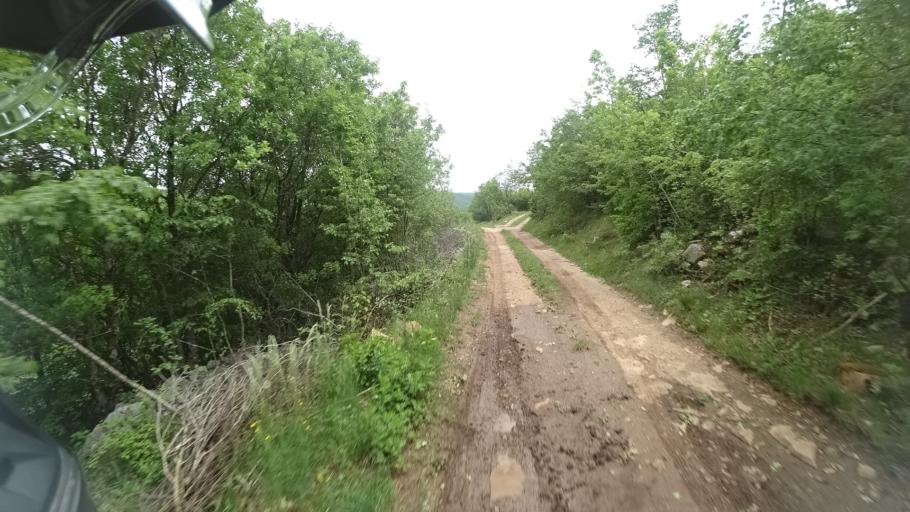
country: HR
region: Splitsko-Dalmatinska
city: Hrvace
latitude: 43.8929
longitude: 16.5510
